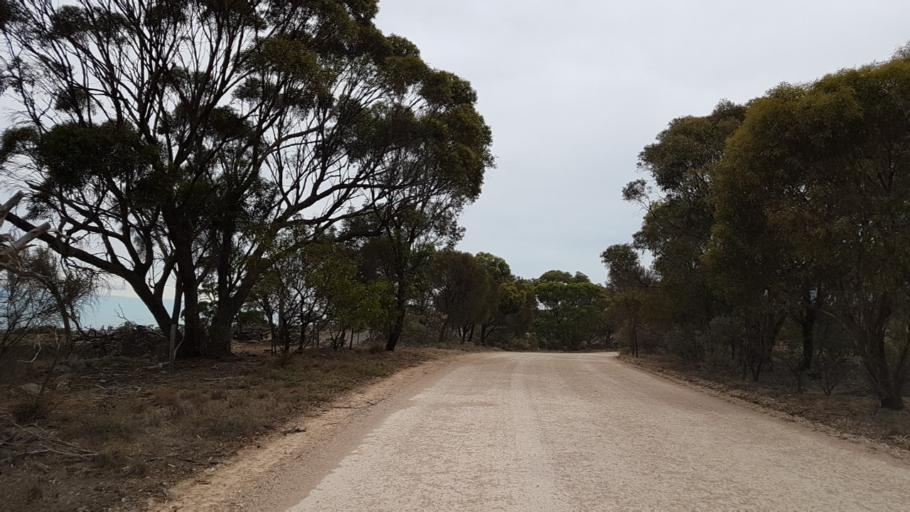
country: AU
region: South Australia
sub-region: Mount Barker
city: Callington
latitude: -35.0067
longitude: 139.0745
